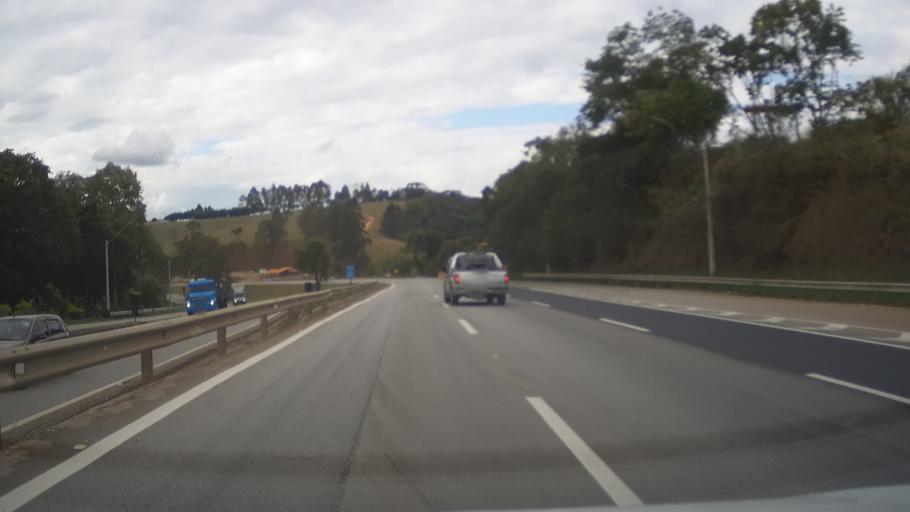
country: BR
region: Minas Gerais
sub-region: Itauna
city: Itauna
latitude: -20.3421
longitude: -44.4409
